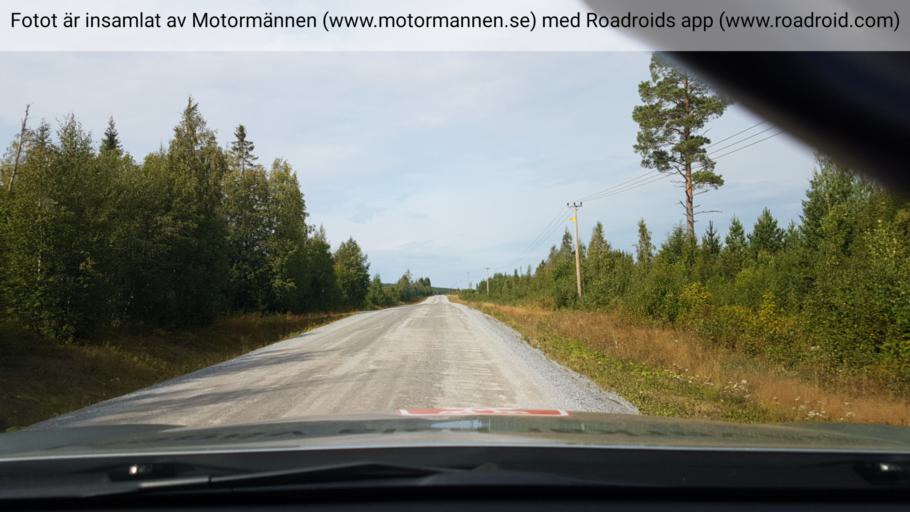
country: SE
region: Vaesterbotten
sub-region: Bjurholms Kommun
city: Bjurholm
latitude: 63.8775
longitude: 19.4447
